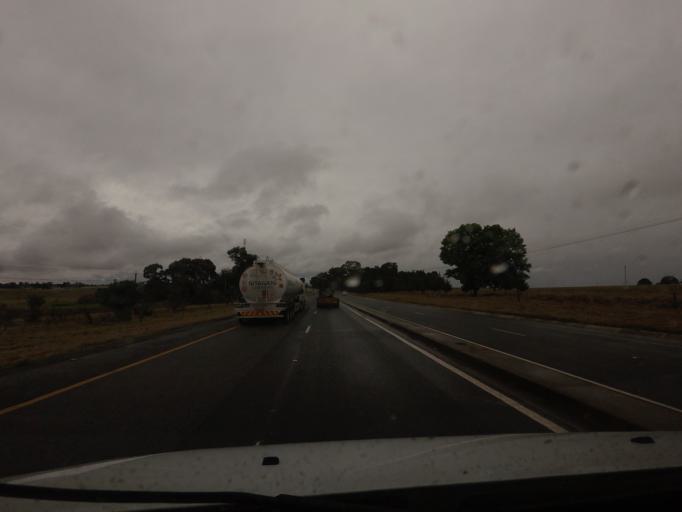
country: ZA
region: Mpumalanga
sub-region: Nkangala District Municipality
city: Belfast
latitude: -25.7478
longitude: 30.0018
